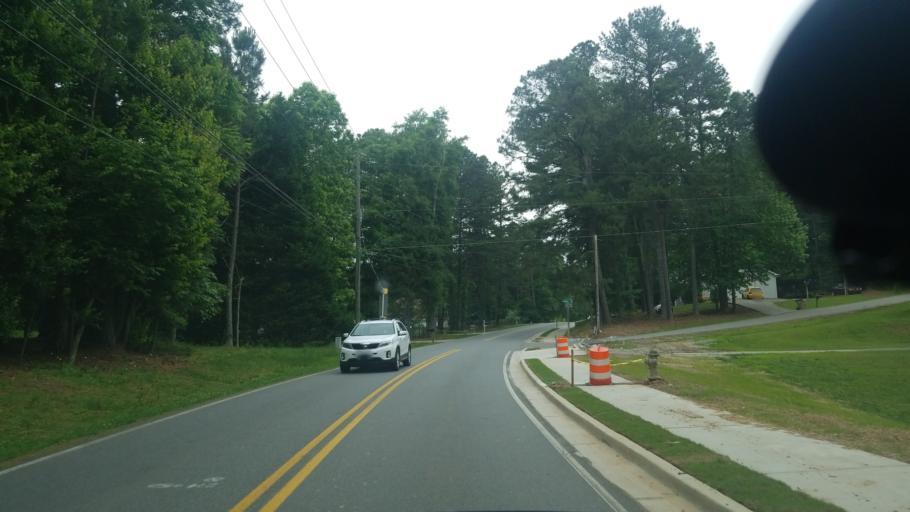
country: US
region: Georgia
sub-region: Forsyth County
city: Cumming
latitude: 34.1360
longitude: -84.1446
